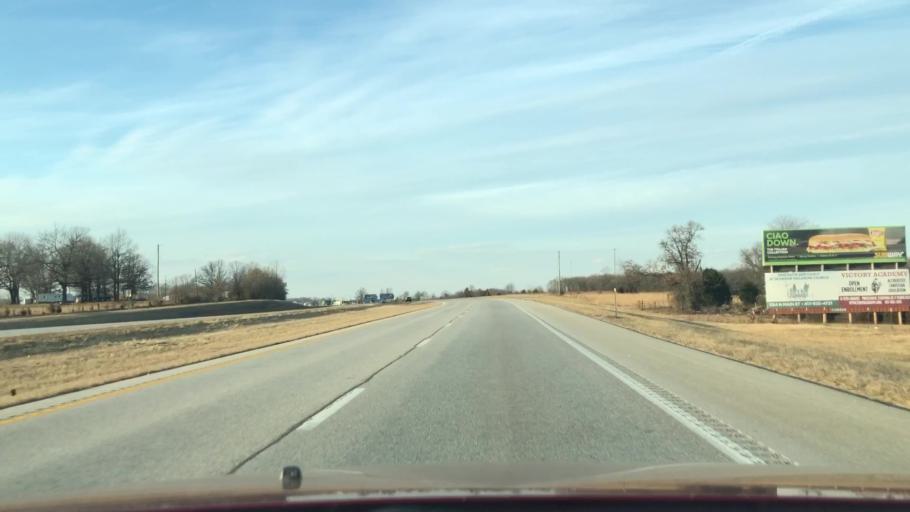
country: US
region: Missouri
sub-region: Webster County
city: Seymour
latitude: 37.1431
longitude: -92.7470
